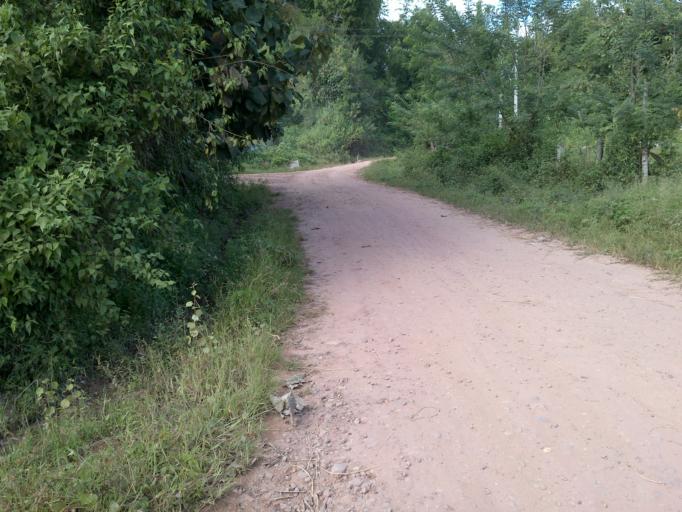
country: TH
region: Nan
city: Chaloem Phra Kiat
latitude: 19.7186
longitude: 101.3423
